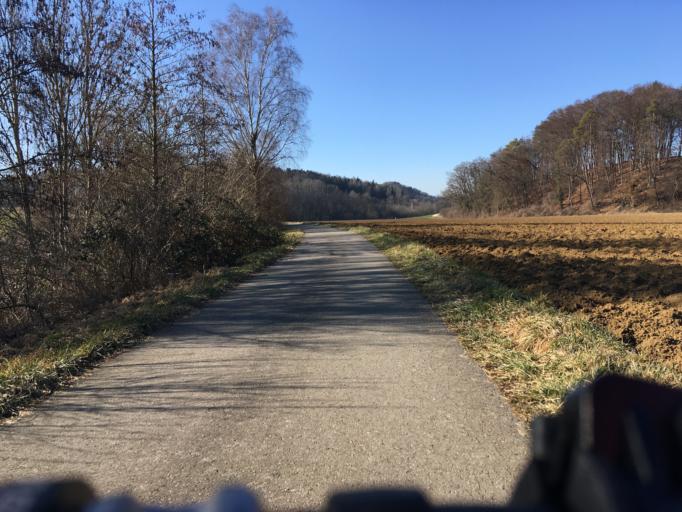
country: DE
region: Baden-Wuerttemberg
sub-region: Freiburg Region
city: Gottmadingen
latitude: 47.7294
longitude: 8.7425
